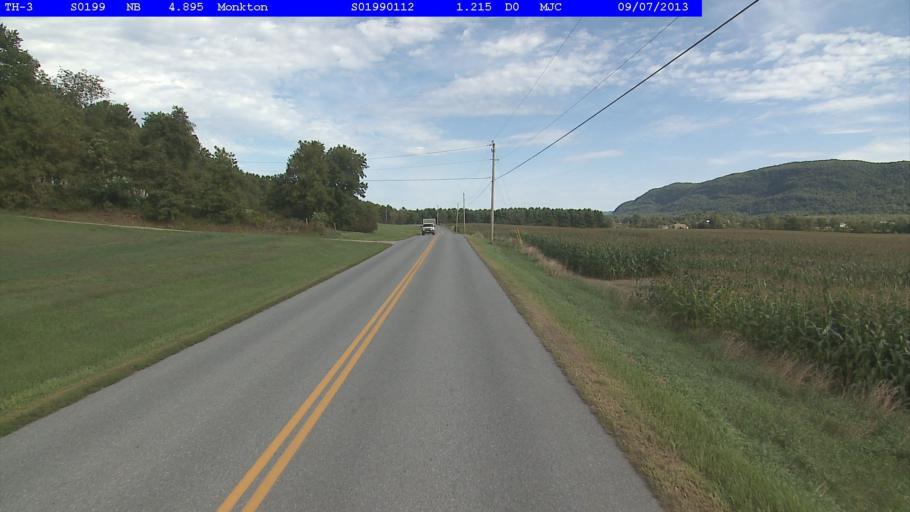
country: US
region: Vermont
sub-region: Addison County
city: Bristol
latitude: 44.1980
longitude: -73.1100
